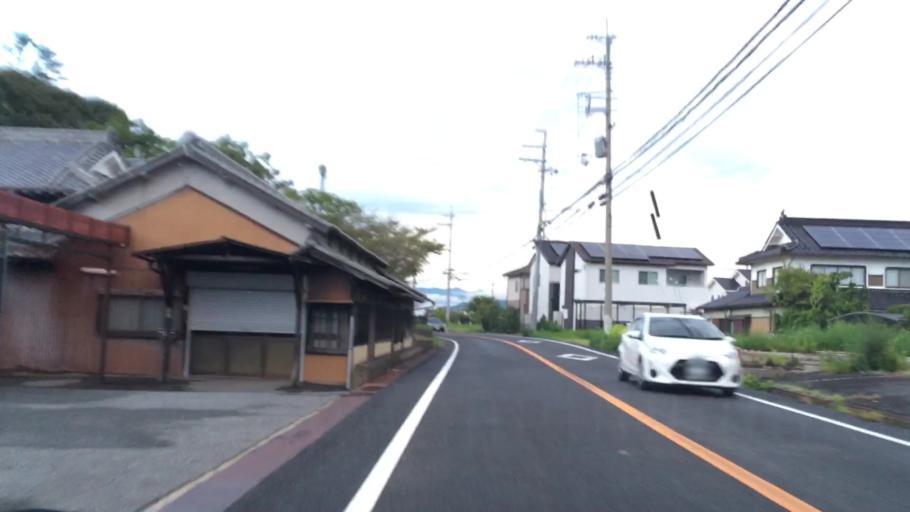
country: JP
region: Hyogo
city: Himeji
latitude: 34.9156
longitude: 134.7407
